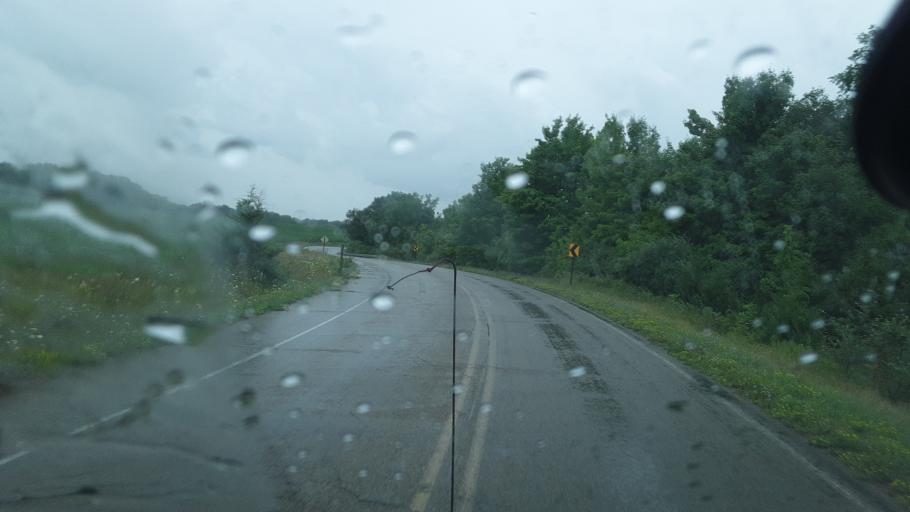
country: US
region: Ohio
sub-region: Williams County
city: Pioneer
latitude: 41.7088
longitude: -84.6515
